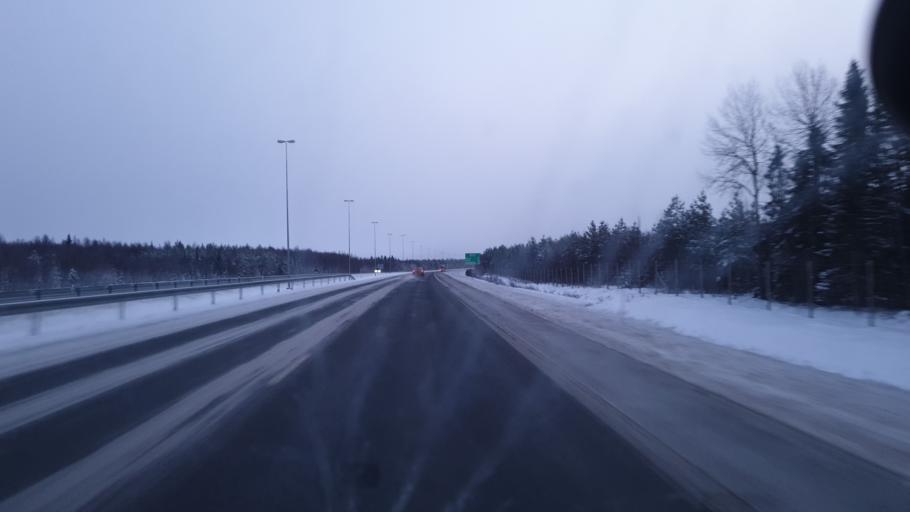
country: FI
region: Lapland
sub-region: Kemi-Tornio
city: Tornio
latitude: 65.8385
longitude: 24.3042
